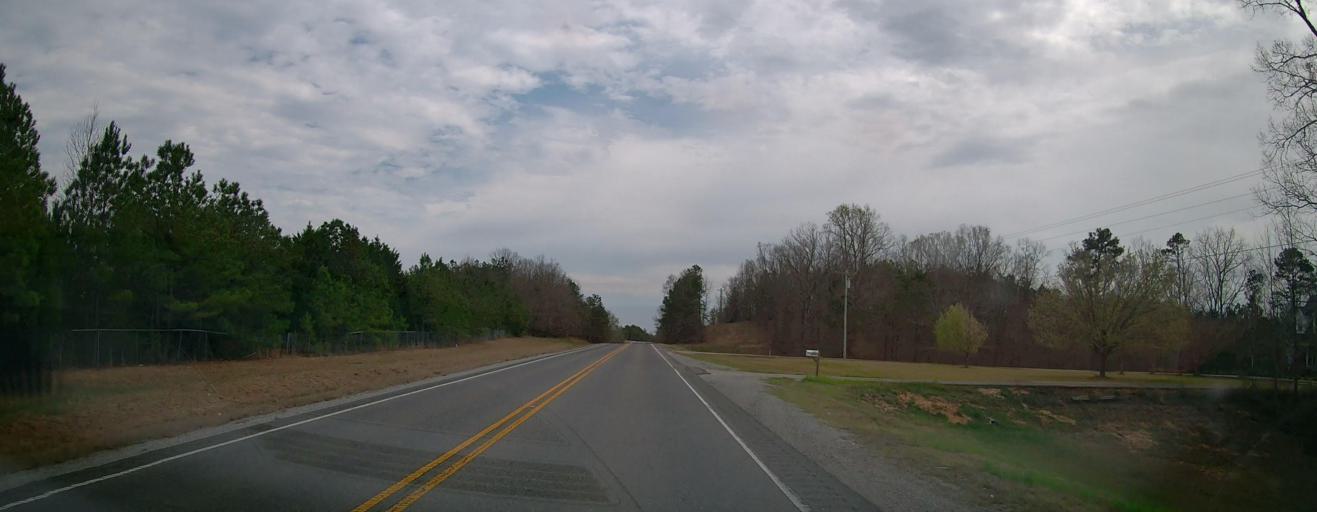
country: US
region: Alabama
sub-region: Marion County
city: Guin
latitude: 34.0341
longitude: -87.9469
